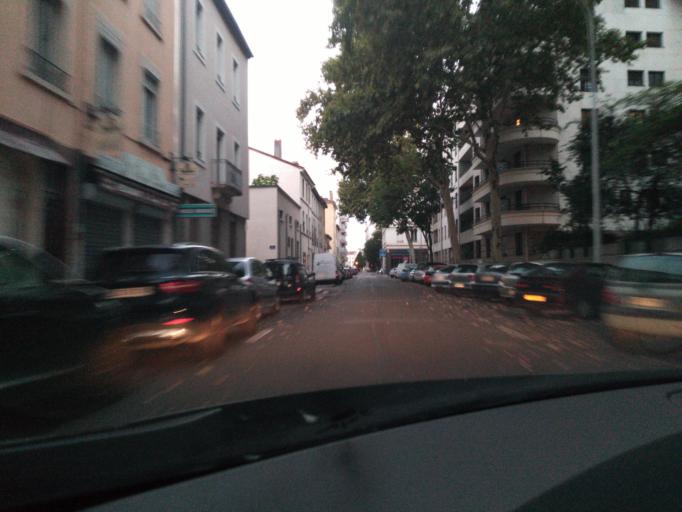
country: FR
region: Rhone-Alpes
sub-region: Departement du Rhone
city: Villeurbanne
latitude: 45.7609
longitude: 4.8664
